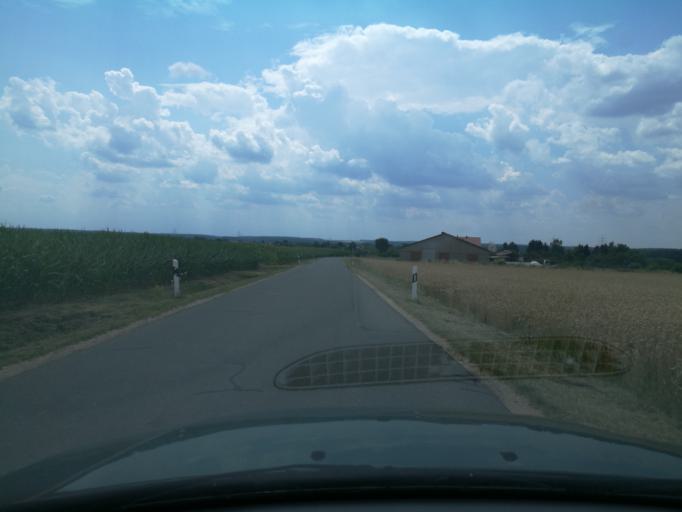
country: DE
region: Bavaria
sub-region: Regierungsbezirk Mittelfranken
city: Grosshabersdorf
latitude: 49.4168
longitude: 10.7808
